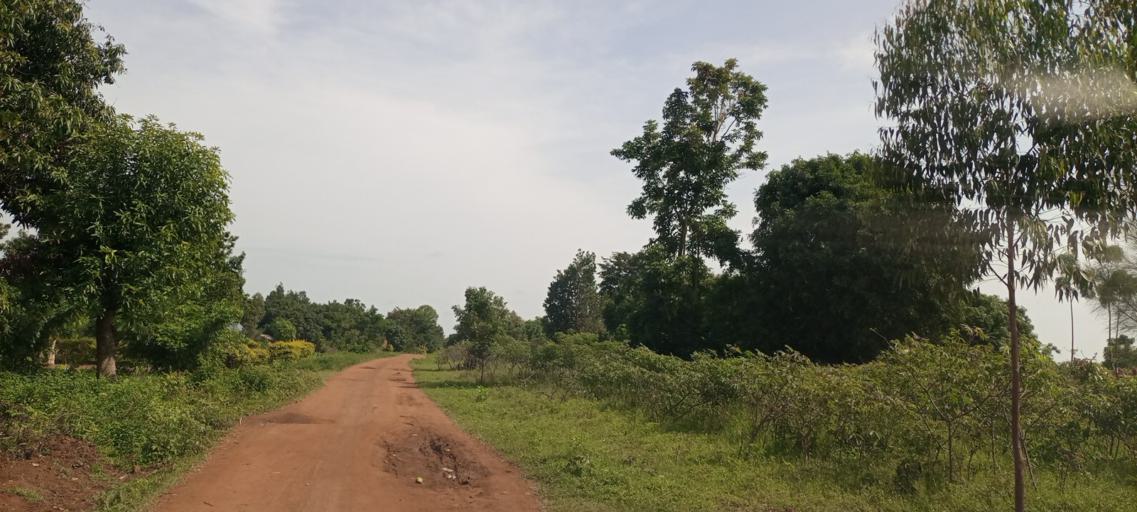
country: UG
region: Eastern Region
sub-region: Mbale District
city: Mbale
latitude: 1.1285
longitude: 34.0253
